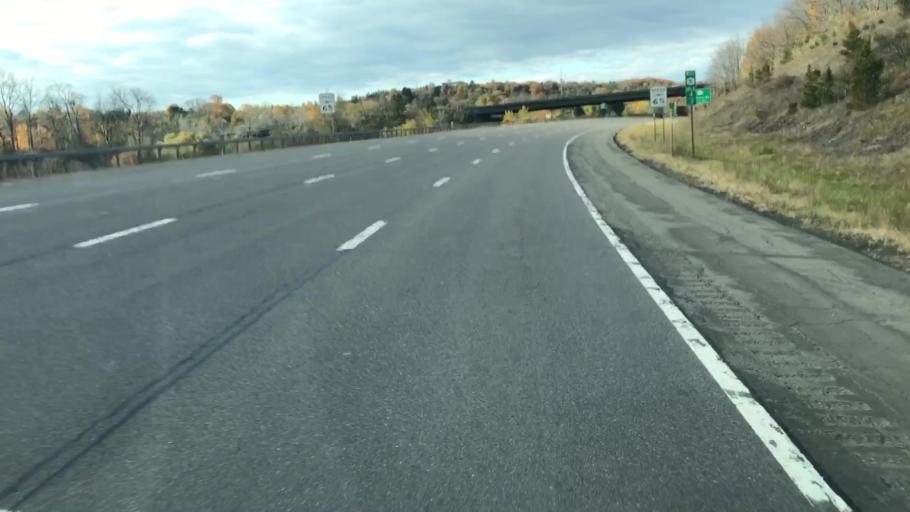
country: US
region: New York
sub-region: Onondaga County
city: Fairmount
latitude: 43.0542
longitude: -76.2408
